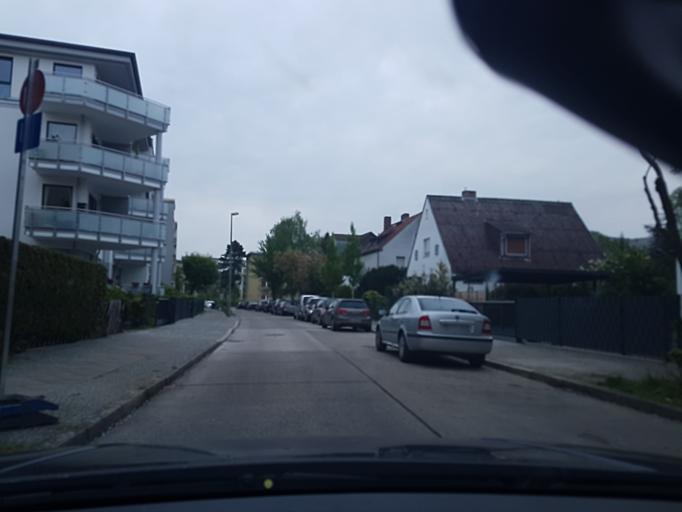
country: DE
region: Berlin
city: Mariendorf
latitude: 52.4356
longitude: 13.3838
